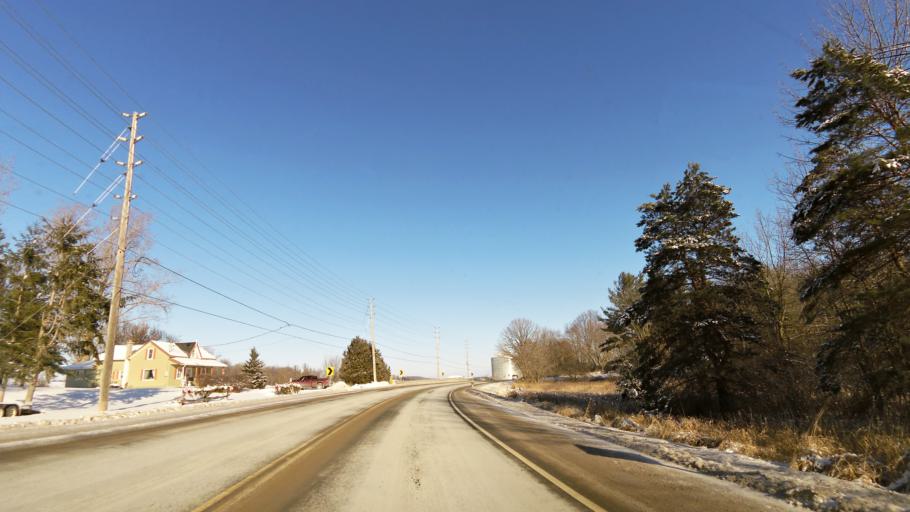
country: CA
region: Ontario
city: Quinte West
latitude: 44.2168
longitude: -77.8281
